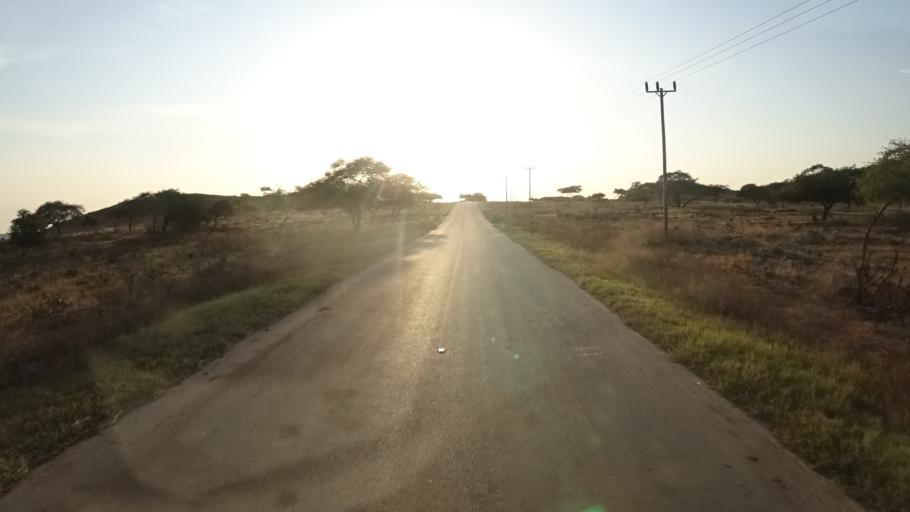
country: OM
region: Zufar
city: Salalah
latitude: 17.1485
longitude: 54.6038
